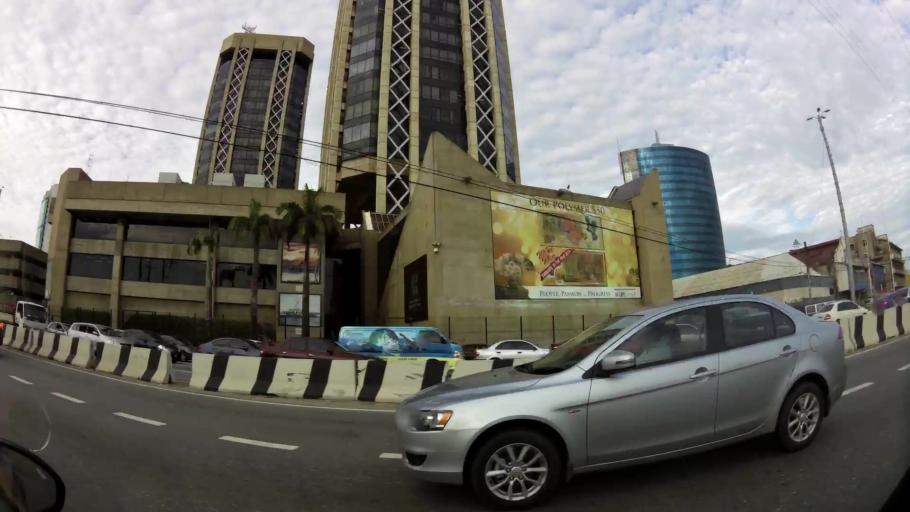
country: TT
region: San Juan/Laventille
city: Laventille
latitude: 10.6480
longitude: -61.5125
